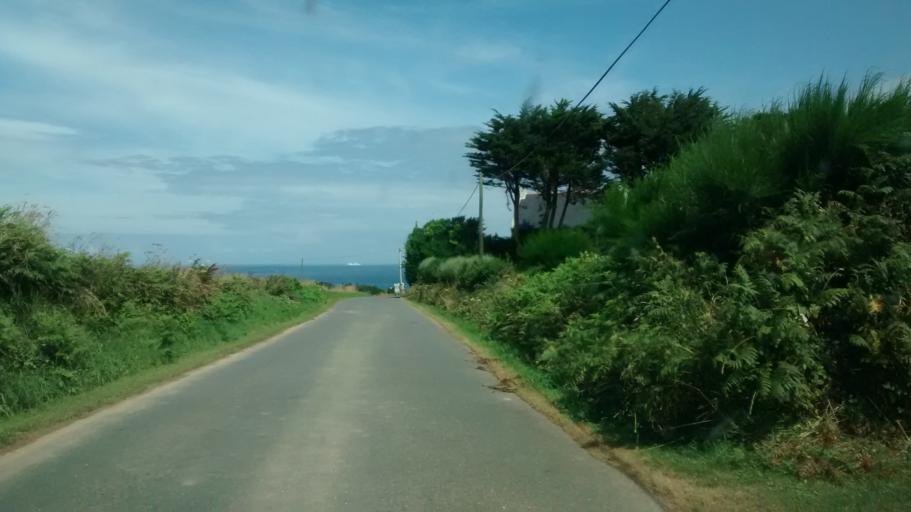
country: FR
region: Brittany
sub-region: Departement du Finistere
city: Plouguerneau
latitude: 48.6186
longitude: -4.4793
